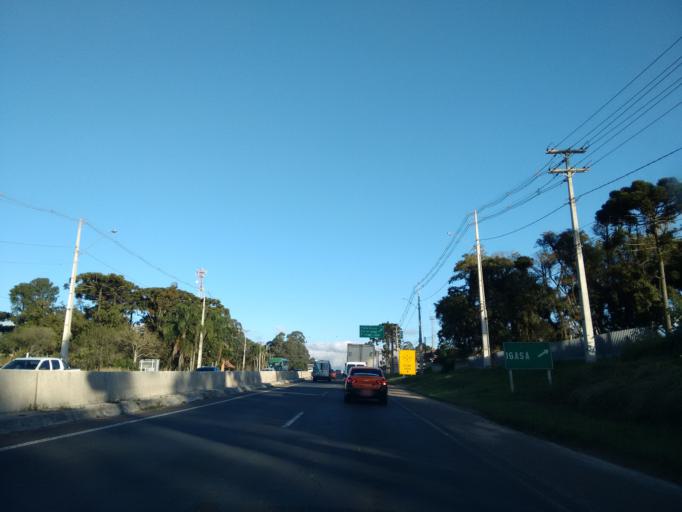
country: BR
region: Parana
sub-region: Sao Jose Dos Pinhais
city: Sao Jose dos Pinhais
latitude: -25.5639
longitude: -49.1836
